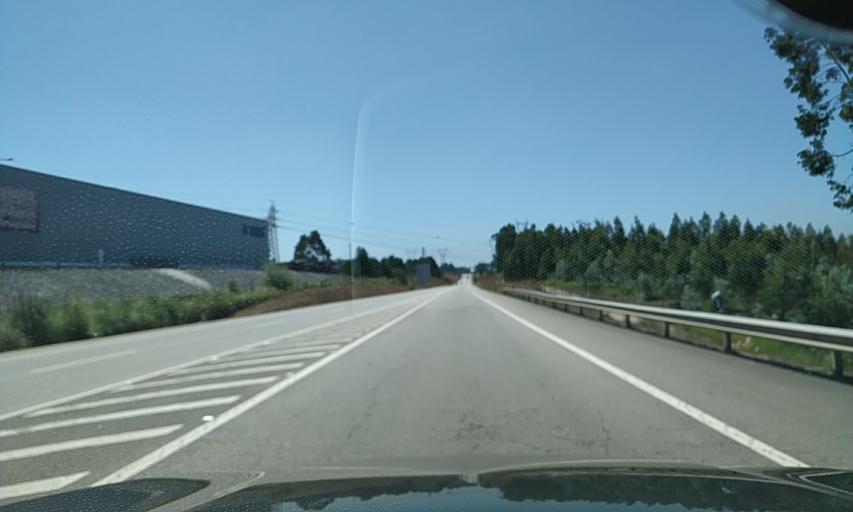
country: PT
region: Aveiro
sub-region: Agueda
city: Agueda
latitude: 40.5892
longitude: -8.4708
